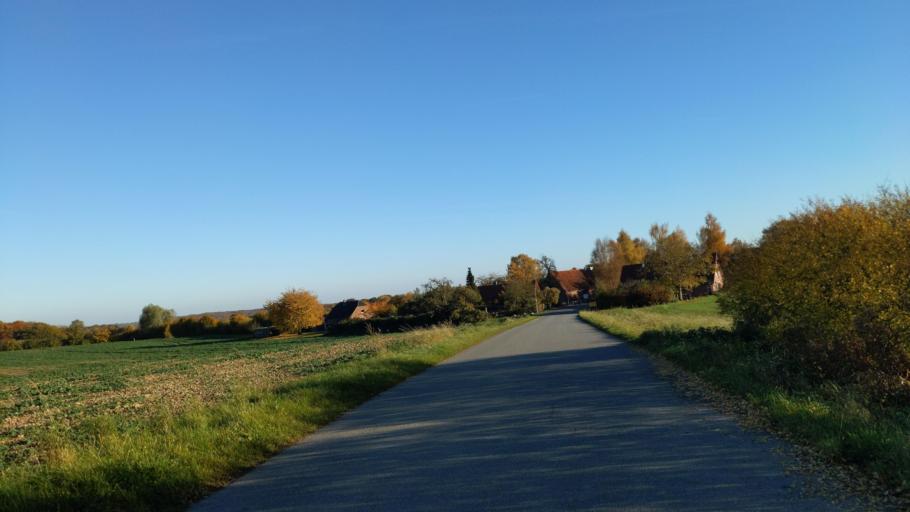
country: DE
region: Schleswig-Holstein
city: Pogeez
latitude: 53.7348
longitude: 10.7094
